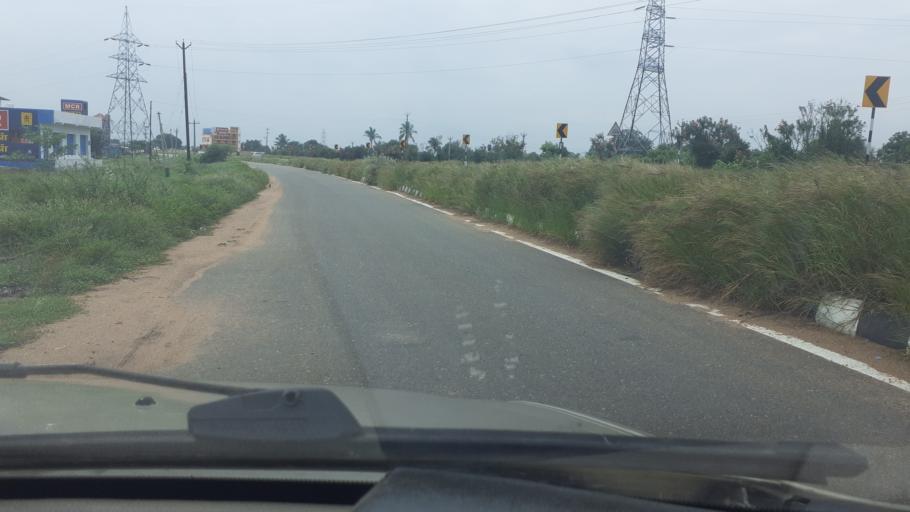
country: IN
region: Tamil Nadu
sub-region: Madurai
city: Tirupparangunram
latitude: 9.8372
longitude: 77.9884
